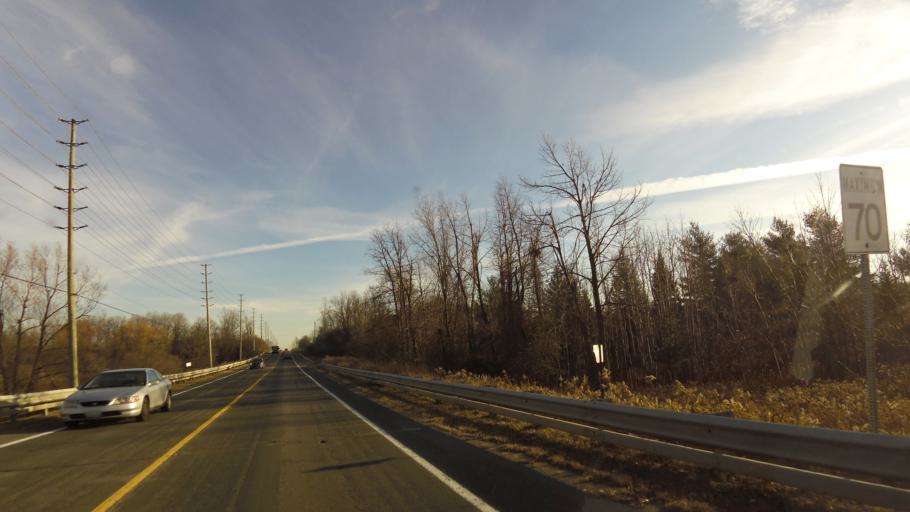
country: CA
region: Ontario
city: Brampton
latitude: 43.7678
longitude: -79.7042
